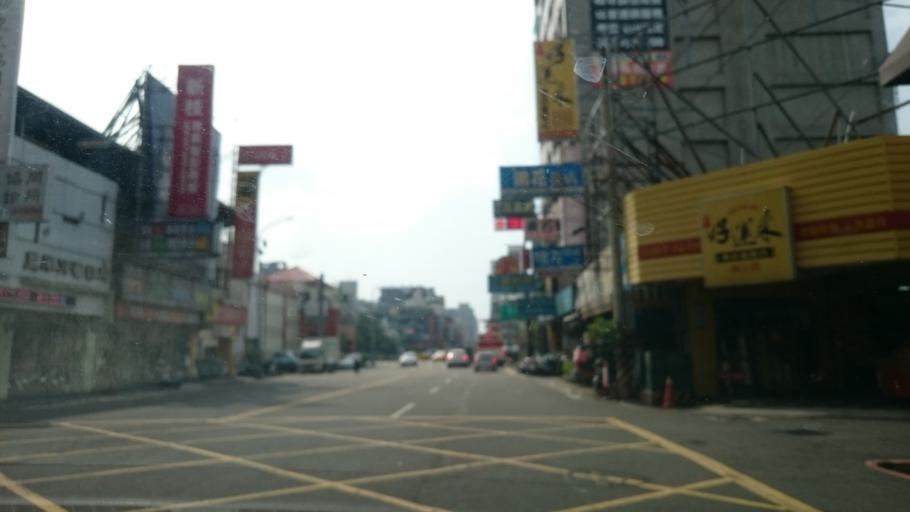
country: TW
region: Taiwan
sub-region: Taichung City
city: Taichung
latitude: 24.1468
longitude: 120.6584
